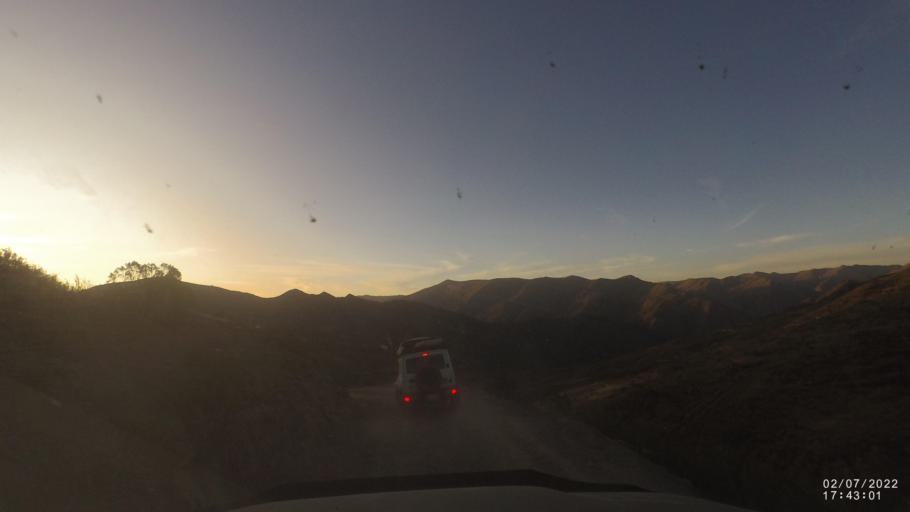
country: BO
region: Cochabamba
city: Irpa Irpa
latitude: -17.8562
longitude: -66.6166
